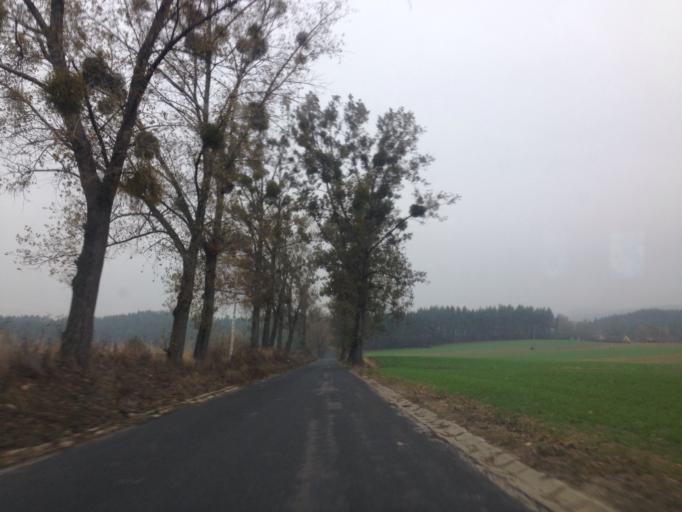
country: PL
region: Kujawsko-Pomorskie
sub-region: Powiat brodnicki
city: Bartniczka
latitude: 53.2422
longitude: 19.5977
